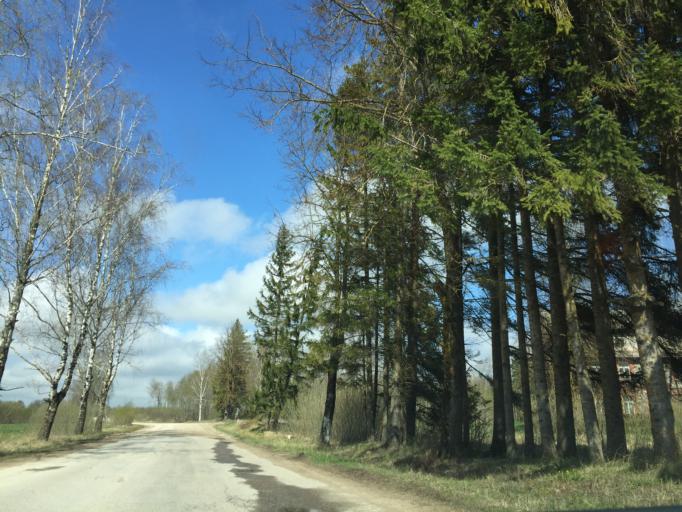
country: LV
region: Apes Novads
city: Ape
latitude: 57.4748
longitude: 26.4696
